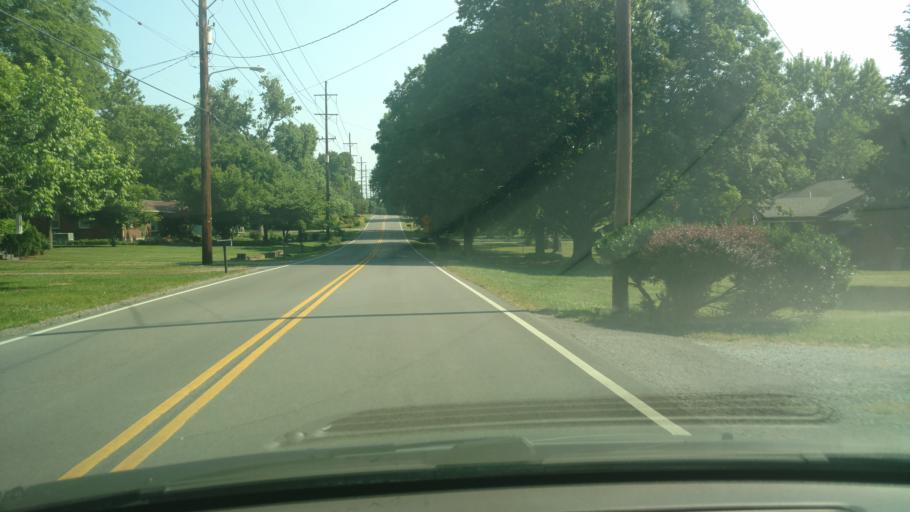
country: US
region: Tennessee
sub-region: Davidson County
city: Nashville
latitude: 36.2245
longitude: -86.7346
